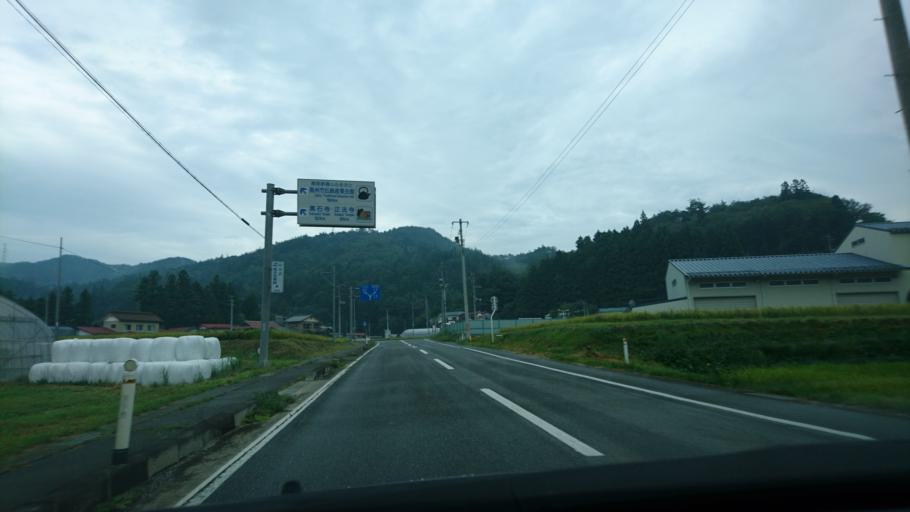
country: JP
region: Iwate
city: Ichinoseki
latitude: 39.0077
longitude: 141.2620
